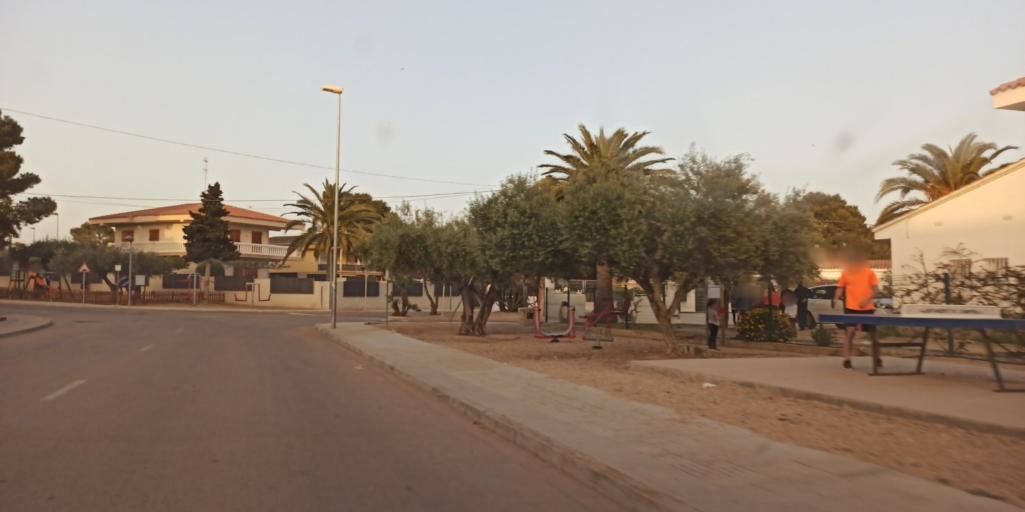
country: ES
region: Catalonia
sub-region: Provincia de Tarragona
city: L'Ampolla
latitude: 40.8227
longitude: 0.7290
